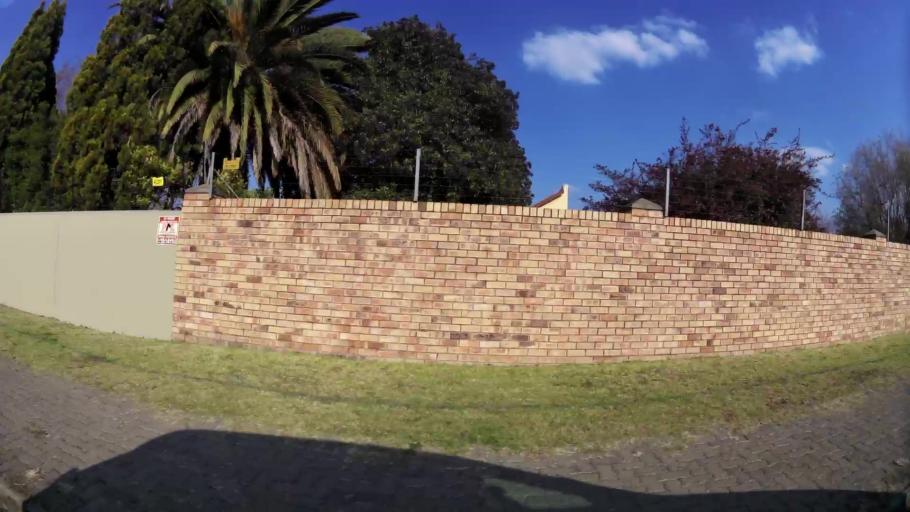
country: ZA
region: Gauteng
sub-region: City of Johannesburg Metropolitan Municipality
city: Modderfontein
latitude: -26.0774
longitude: 28.2071
